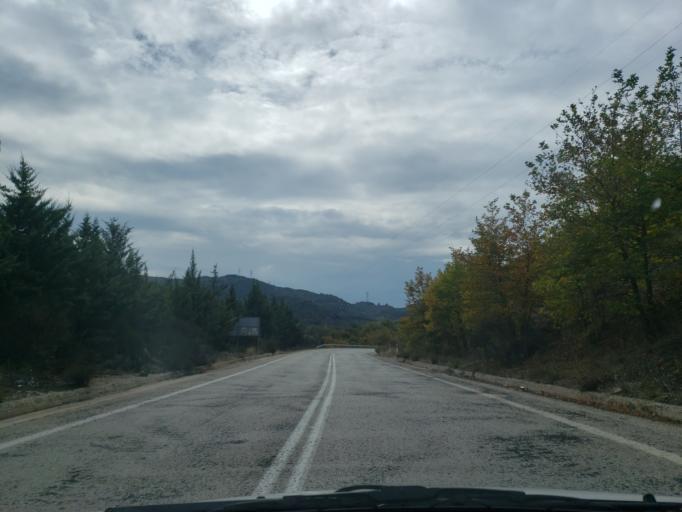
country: GR
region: Central Greece
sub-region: Nomos Fthiotidos
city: Stavros
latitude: 39.0055
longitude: 22.3750
